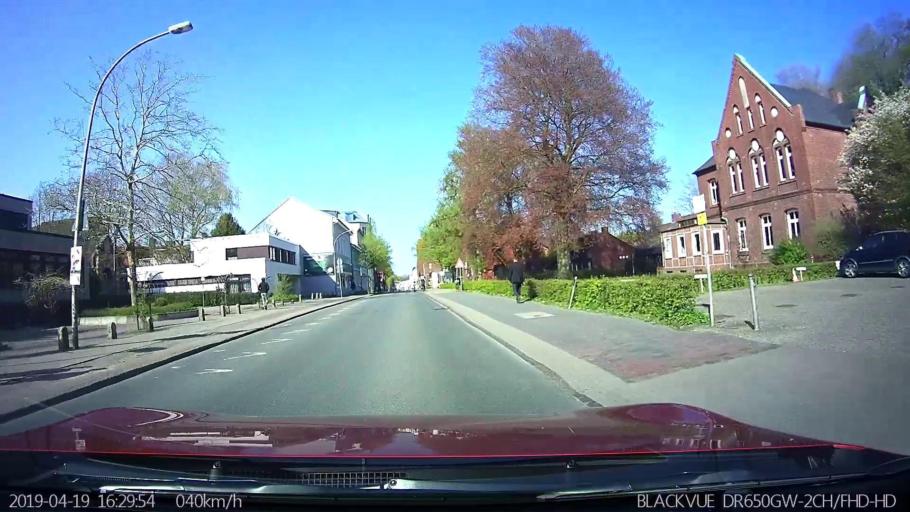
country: DE
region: Schleswig-Holstein
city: Pinneberg
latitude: 53.6574
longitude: 9.7990
